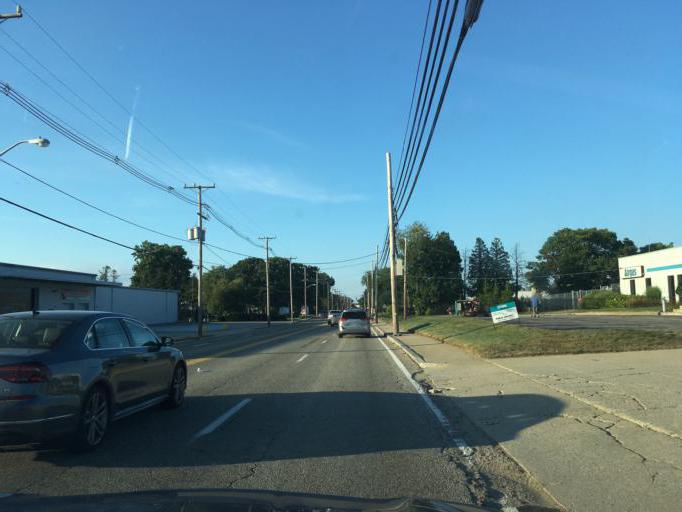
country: US
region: Rhode Island
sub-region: Kent County
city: Warwick
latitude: 41.7329
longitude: -71.4415
